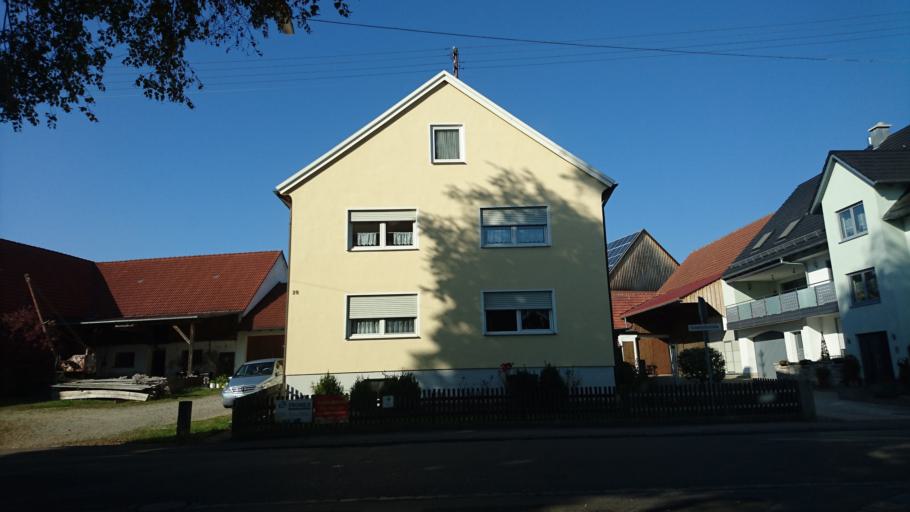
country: DE
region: Bavaria
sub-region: Swabia
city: Zusmarshausen
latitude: 48.4167
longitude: 10.5854
